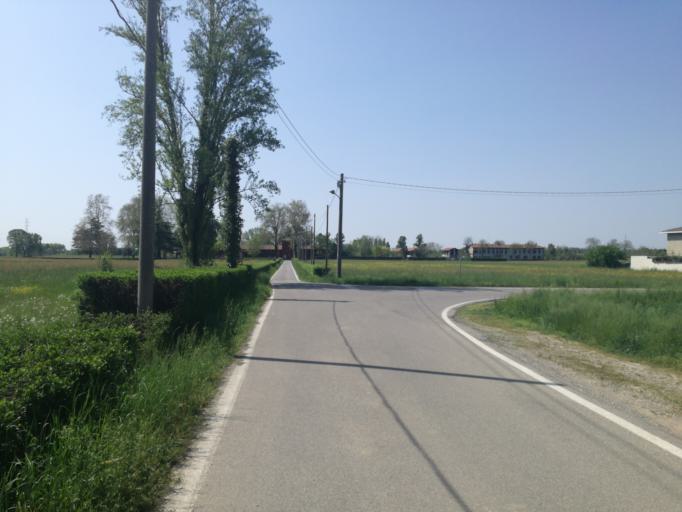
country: IT
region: Lombardy
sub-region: Provincia di Lecco
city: Verderio Superiore
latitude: 45.6579
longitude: 9.4458
